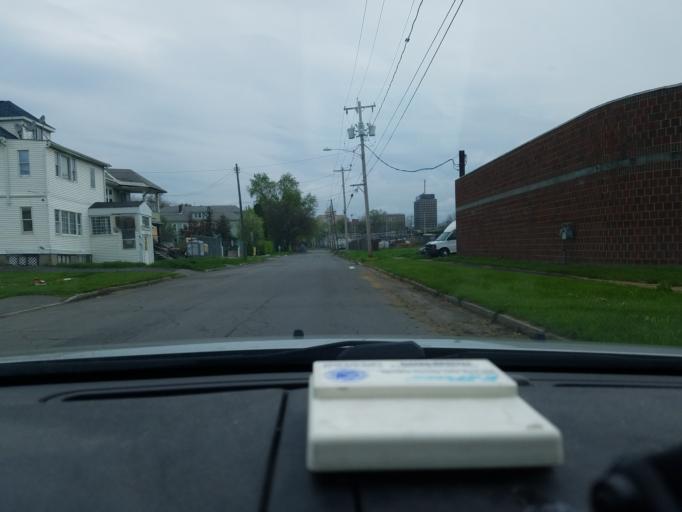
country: US
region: New York
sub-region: Onondaga County
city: Syracuse
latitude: 43.0371
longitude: -76.1529
